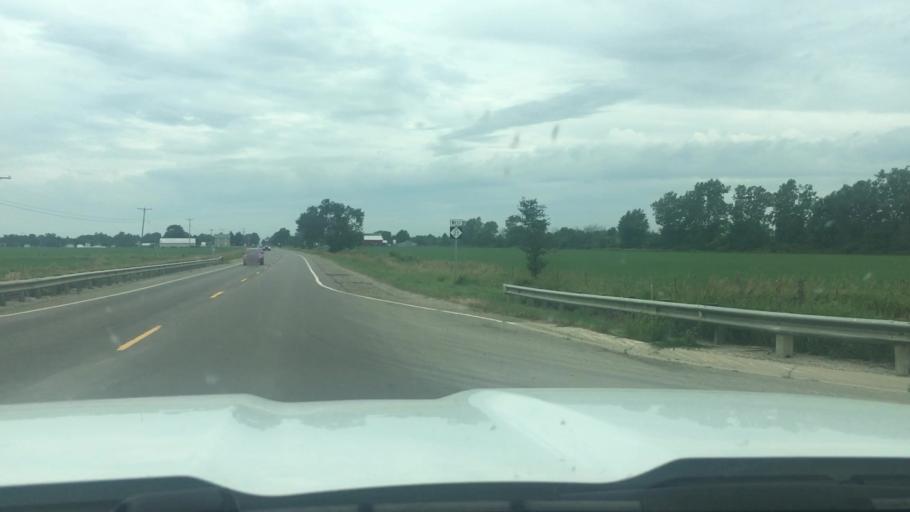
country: US
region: Michigan
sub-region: Clinton County
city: Fowler
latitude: 43.0019
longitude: -84.7199
